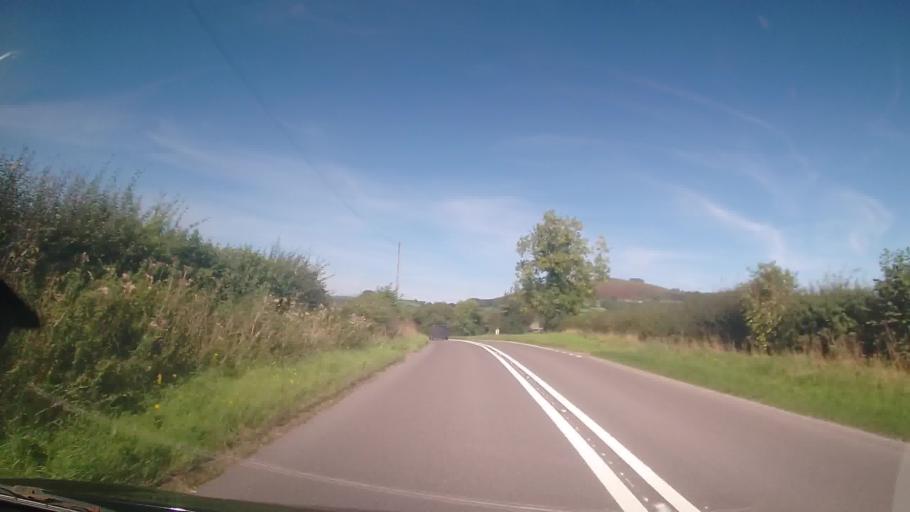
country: GB
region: England
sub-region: Shropshire
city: Lydham
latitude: 52.5174
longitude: -2.9822
